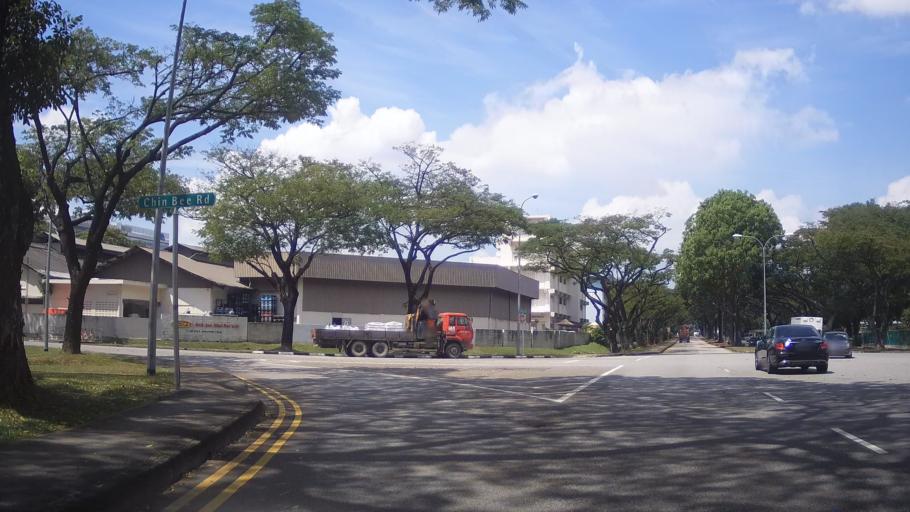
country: SG
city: Singapore
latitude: 1.3292
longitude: 103.7134
